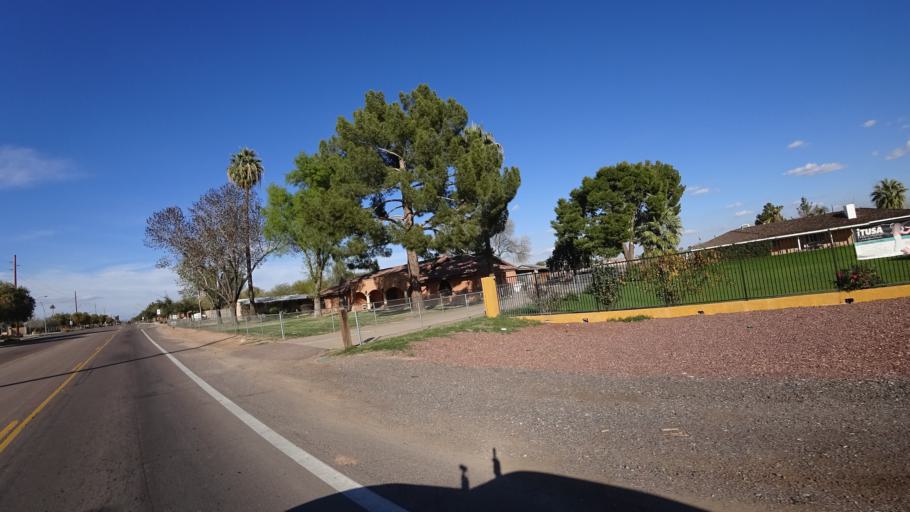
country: US
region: Arizona
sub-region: Maricopa County
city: Peoria
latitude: 33.5405
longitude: -112.2376
